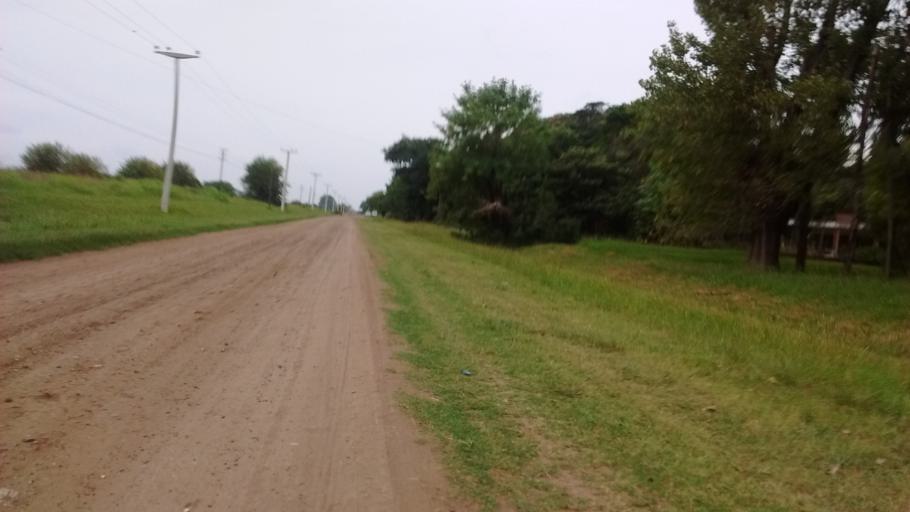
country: AR
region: Santa Fe
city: Funes
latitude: -32.9118
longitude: -60.8412
